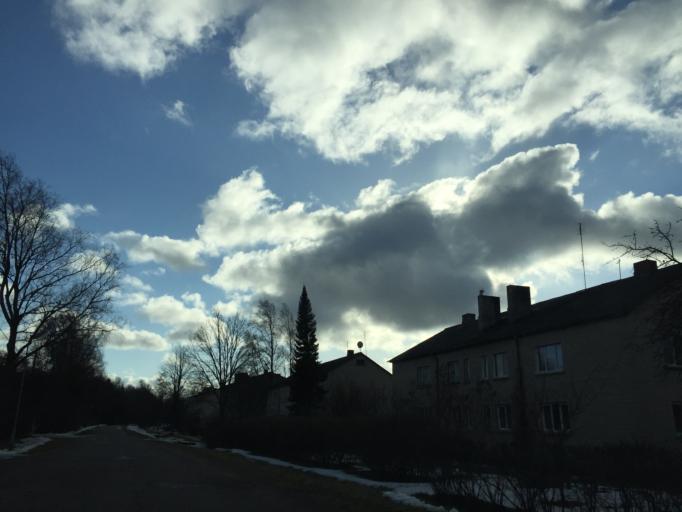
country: LV
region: Limbazu Rajons
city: Limbazi
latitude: 57.6149
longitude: 24.6098
